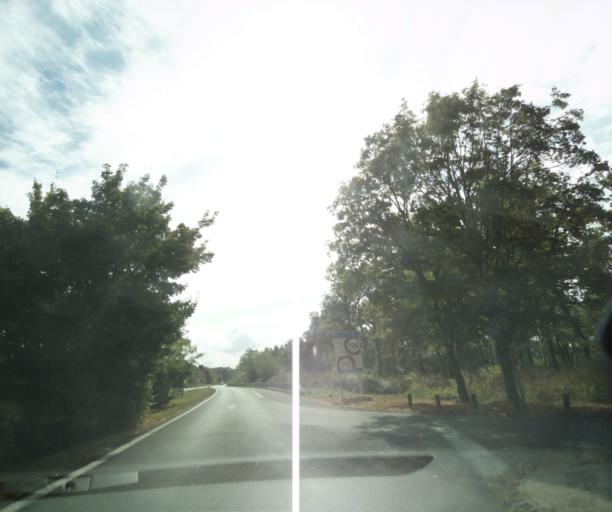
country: FR
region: Poitou-Charentes
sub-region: Departement de la Charente-Maritime
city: Pons
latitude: 45.6089
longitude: -0.5981
